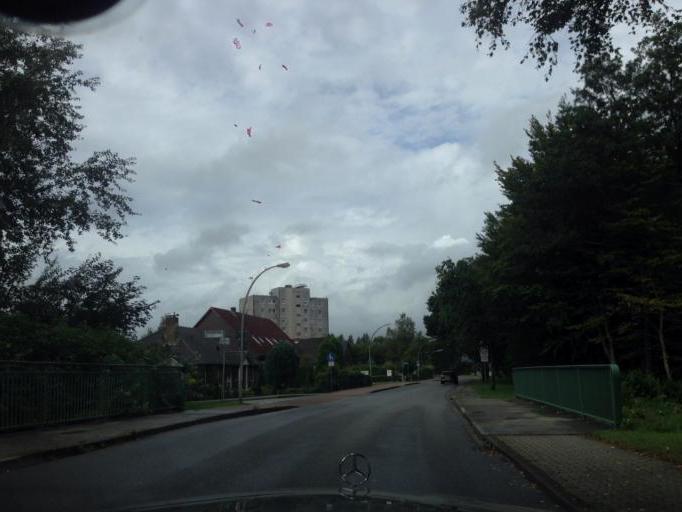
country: DE
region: Schleswig-Holstein
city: Leck
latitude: 54.7744
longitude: 8.9629
